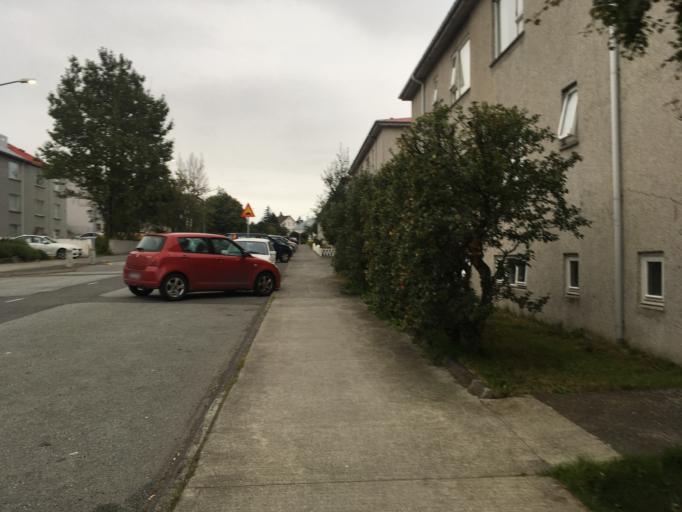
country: IS
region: Capital Region
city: Reykjavik
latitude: 64.1401
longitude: -21.9096
